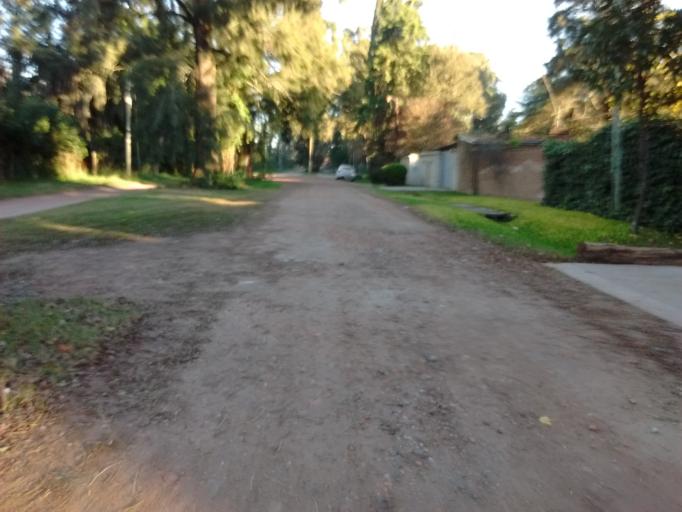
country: AR
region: Santa Fe
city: Funes
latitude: -32.9158
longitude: -60.8329
